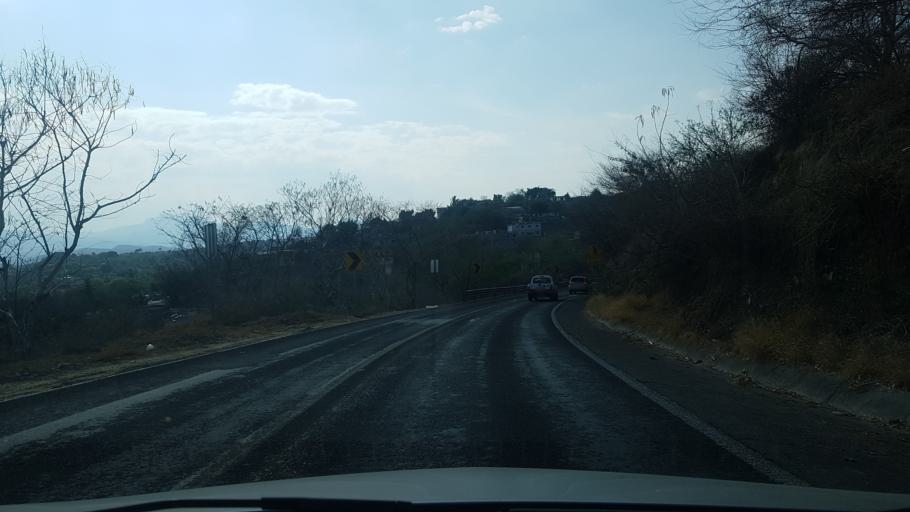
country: MX
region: Morelos
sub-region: Amacuzac
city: Amacuzac
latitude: 18.6027
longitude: -99.3662
